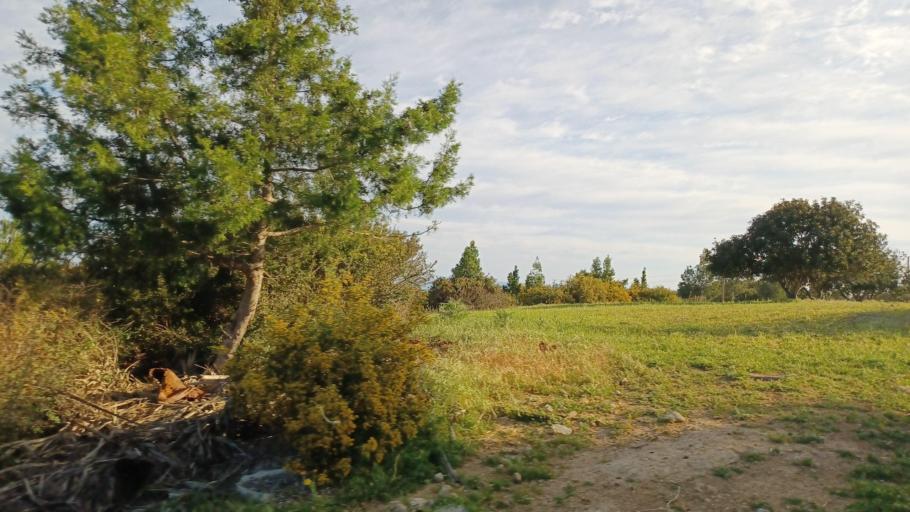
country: CY
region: Pafos
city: Polis
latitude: 35.0347
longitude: 32.3863
